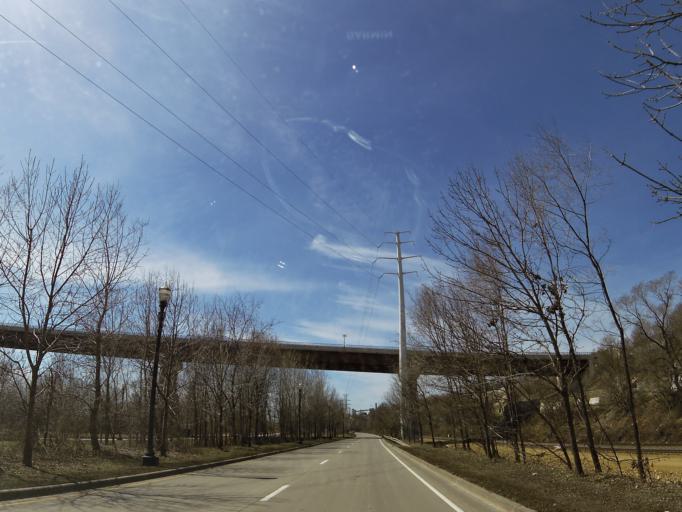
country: US
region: Minnesota
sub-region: Ramsey County
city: Saint Paul
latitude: 44.9371
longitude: -93.1068
